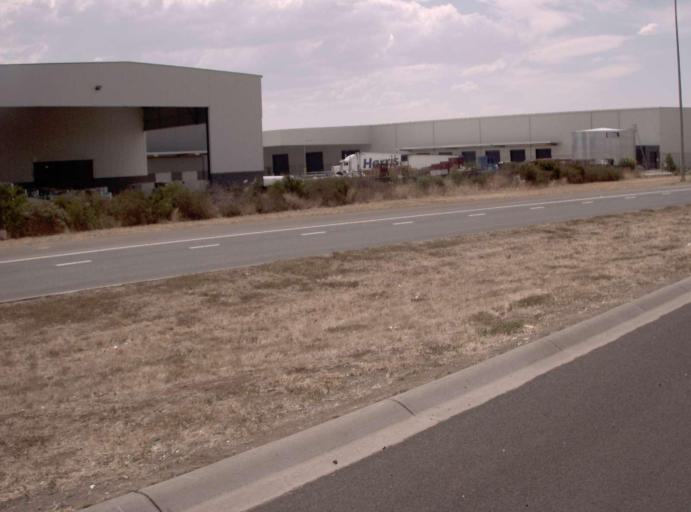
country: AU
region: Victoria
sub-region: Brimbank
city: Derrimut
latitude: -37.7916
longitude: 144.7873
